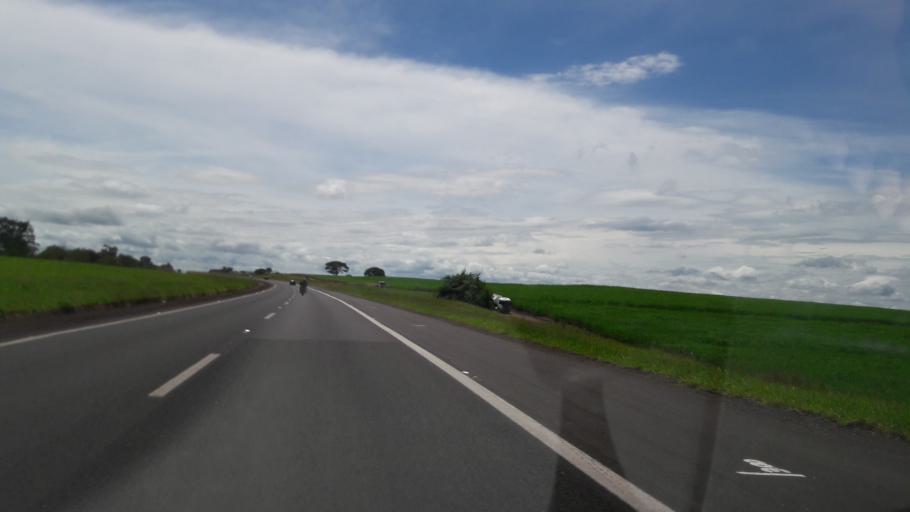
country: BR
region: Sao Paulo
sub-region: Avare
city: Avare
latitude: -22.9406
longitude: -48.9108
